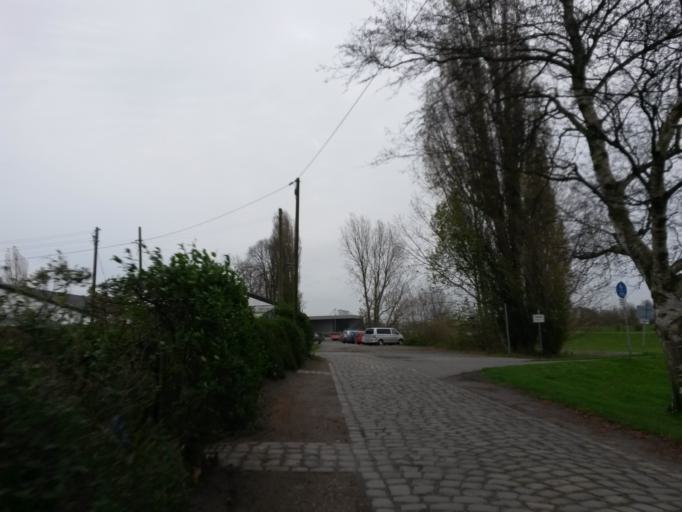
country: DE
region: Bremen
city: Bremen
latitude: 53.0544
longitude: 8.8709
